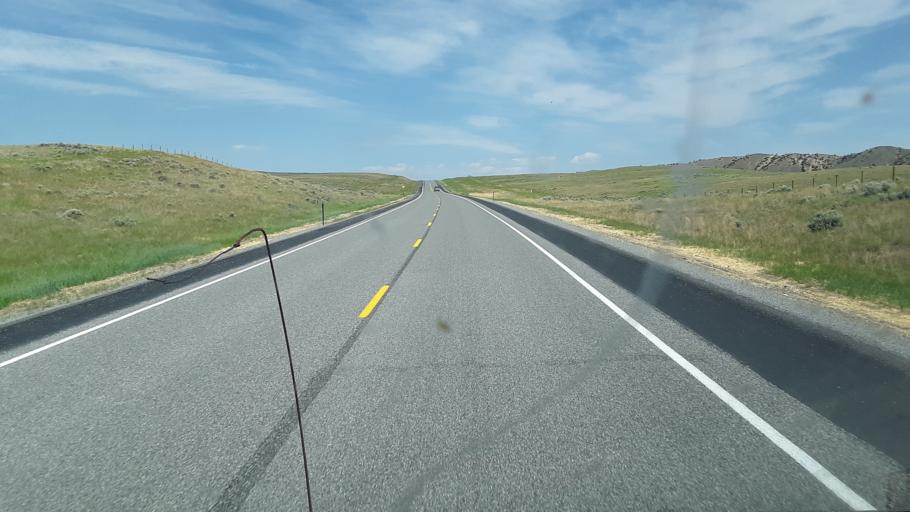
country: US
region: Wyoming
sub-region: Park County
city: Cody
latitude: 44.2812
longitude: -108.8934
